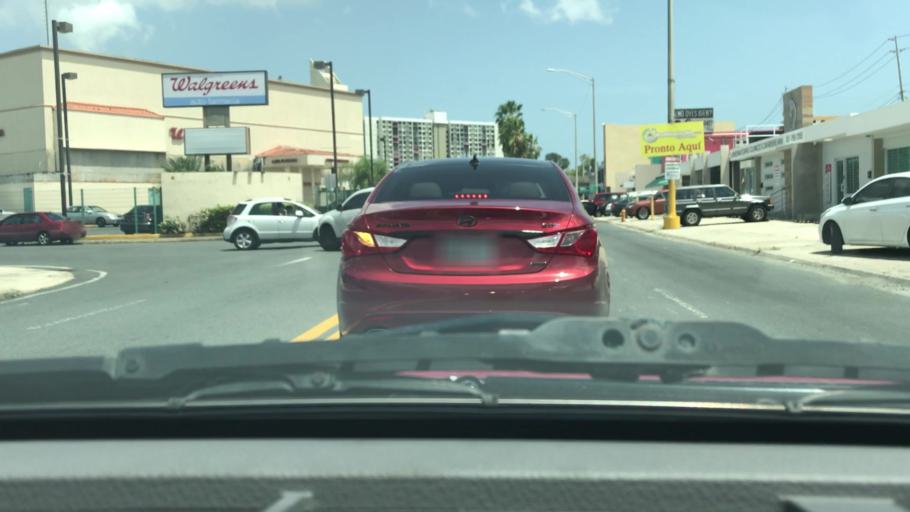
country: PR
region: Bayamon
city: Bayamon
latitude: 18.3932
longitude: -66.1427
